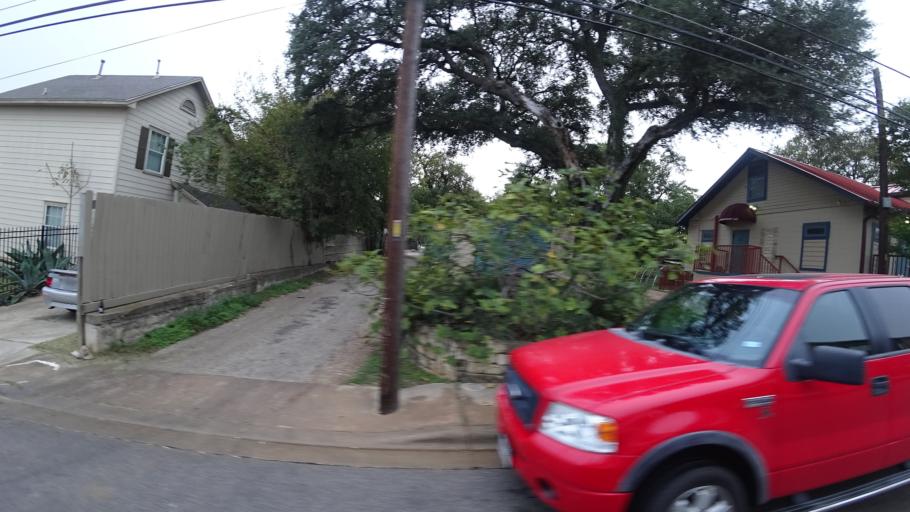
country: US
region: Texas
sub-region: Travis County
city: Austin
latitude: 30.2631
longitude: -97.7151
